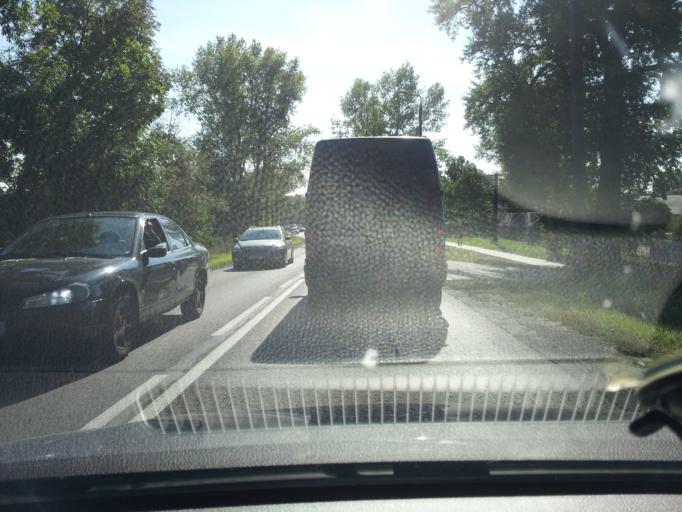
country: PL
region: Kujawsko-Pomorskie
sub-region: Powiat torunski
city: Lubicz Dolny
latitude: 53.0477
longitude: 18.7025
